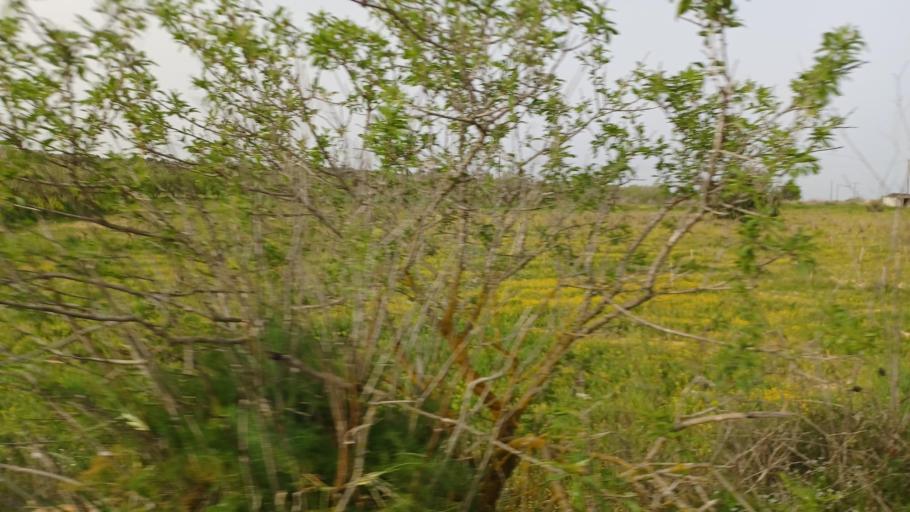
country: CY
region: Pafos
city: Pegeia
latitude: 34.9443
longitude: 32.3771
